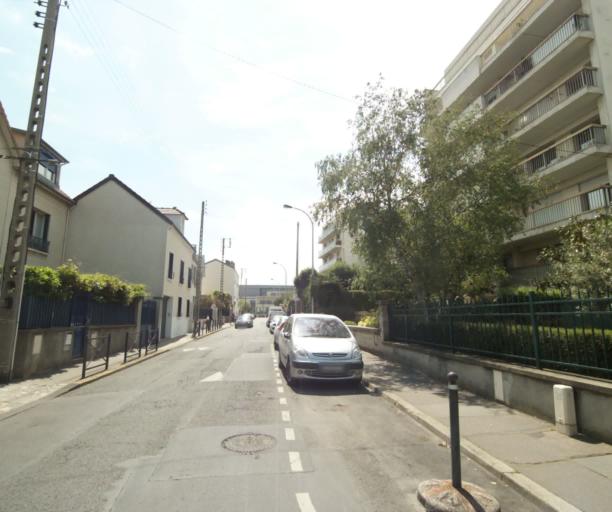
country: FR
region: Ile-de-France
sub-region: Departement des Hauts-de-Seine
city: Colombes
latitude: 48.9117
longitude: 2.2611
